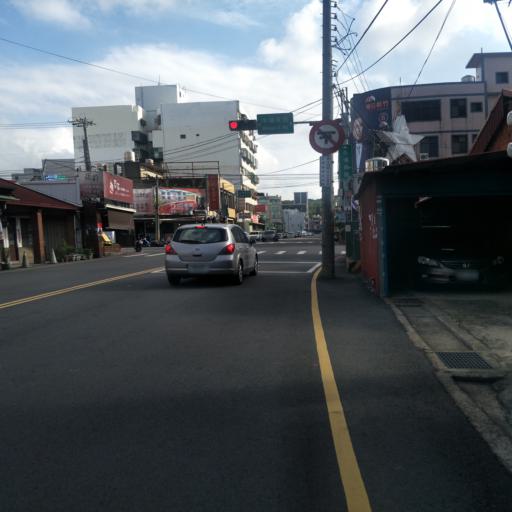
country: TW
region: Taiwan
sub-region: Hsinchu
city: Hsinchu
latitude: 24.7956
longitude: 120.9413
